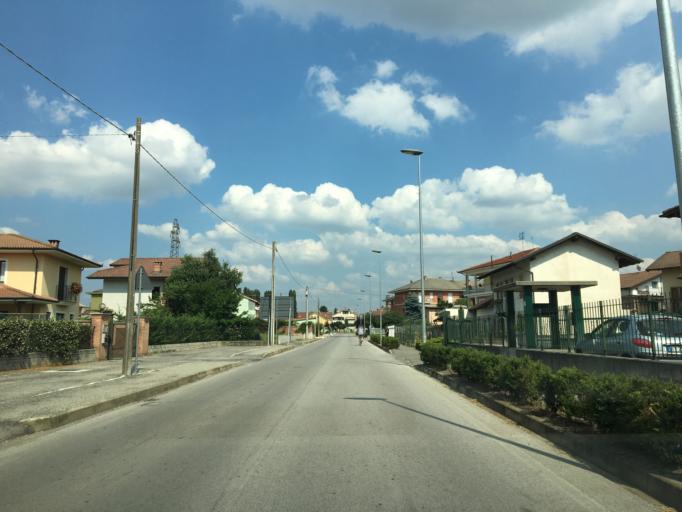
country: IT
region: Piedmont
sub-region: Provincia di Cuneo
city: Sommariva del Bosco
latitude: 44.7724
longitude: 7.7708
